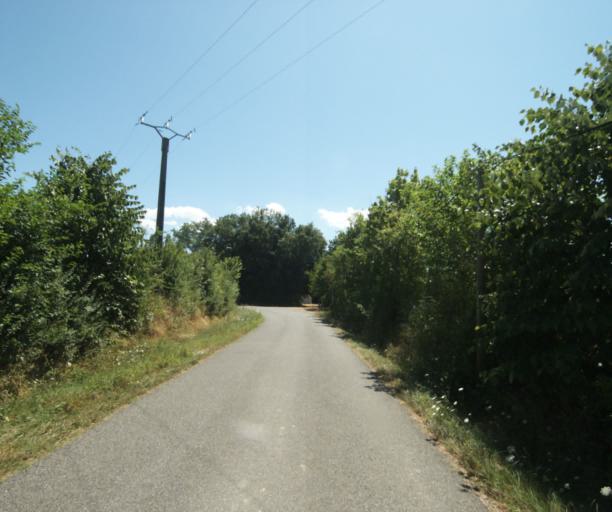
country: FR
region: Midi-Pyrenees
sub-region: Departement de la Haute-Garonne
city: Revel
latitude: 43.4583
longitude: 1.9461
